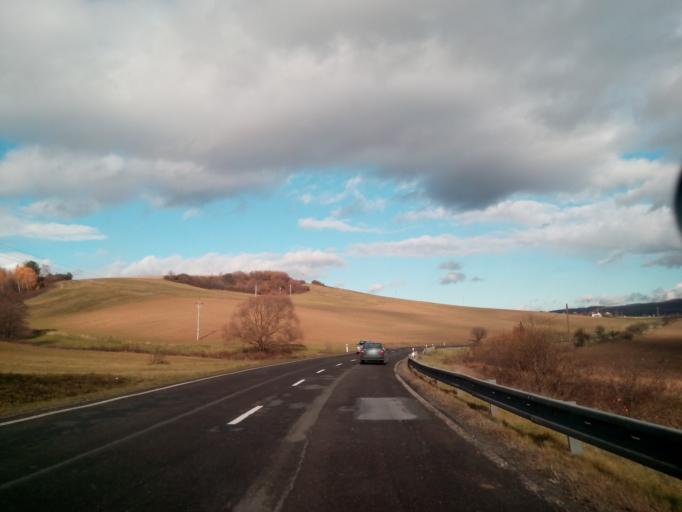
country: SK
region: Presovsky
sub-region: Okres Bardejov
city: Bardejov
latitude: 49.1762
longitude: 21.3061
